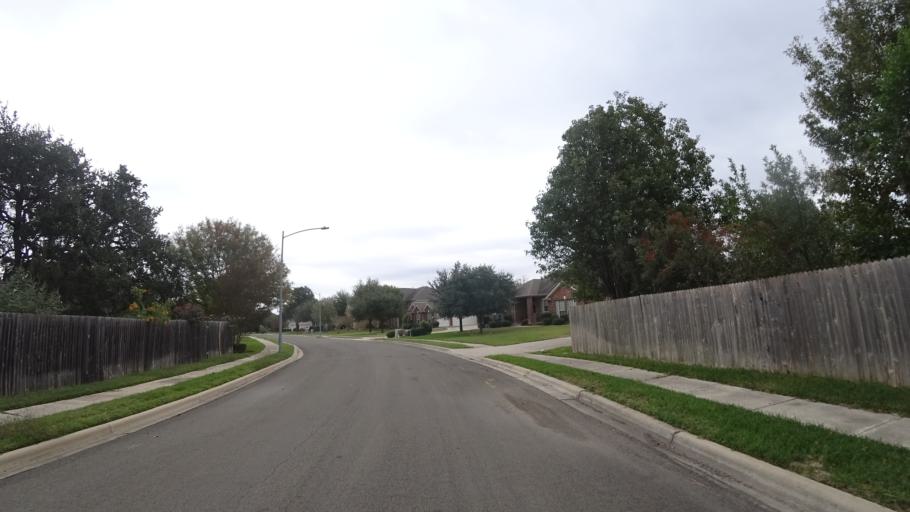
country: US
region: Texas
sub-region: Travis County
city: Shady Hollow
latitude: 30.1535
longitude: -97.8612
